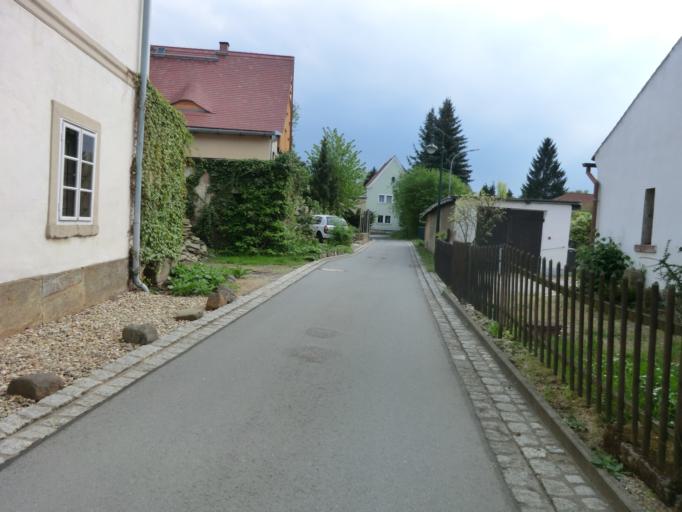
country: DE
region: Saxony
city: Grossschonau
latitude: 50.8958
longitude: 14.6616
